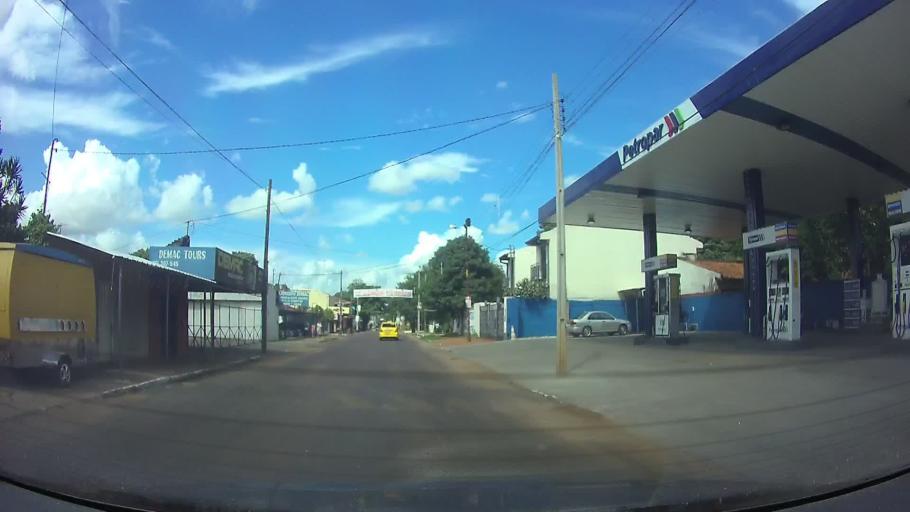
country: PY
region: Central
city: Villa Elisa
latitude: -25.3429
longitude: -57.5768
